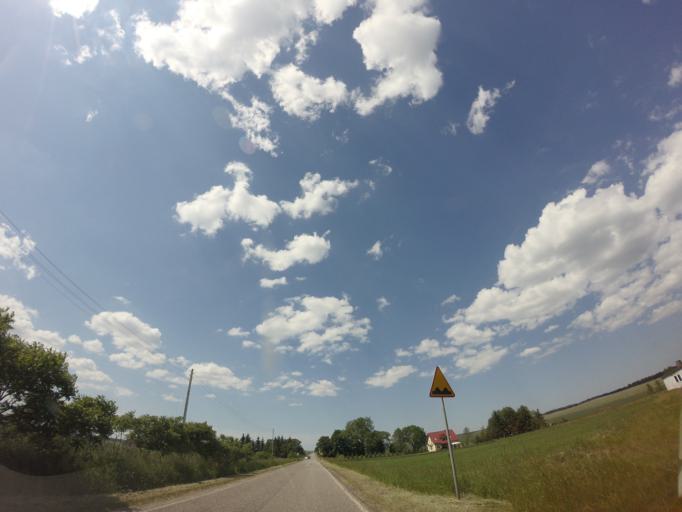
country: PL
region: West Pomeranian Voivodeship
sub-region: Powiat stargardzki
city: Dolice
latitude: 53.1624
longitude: 15.2317
